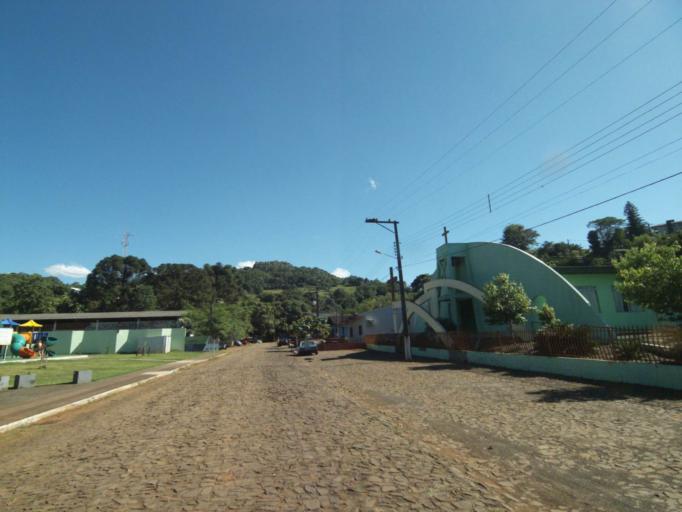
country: BR
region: Parana
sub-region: Ampere
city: Ampere
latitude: -26.1751
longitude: -53.3622
